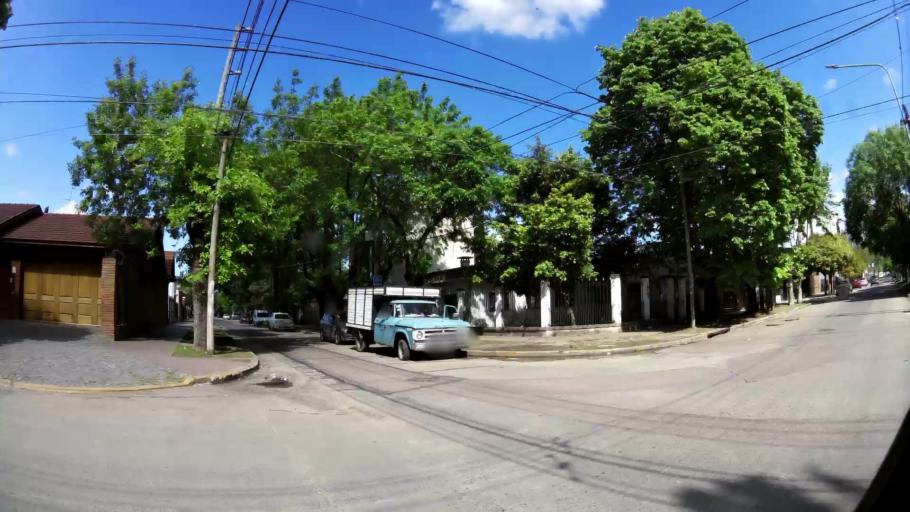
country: AR
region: Buenos Aires
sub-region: Partido de Quilmes
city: Quilmes
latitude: -34.8067
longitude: -58.2730
